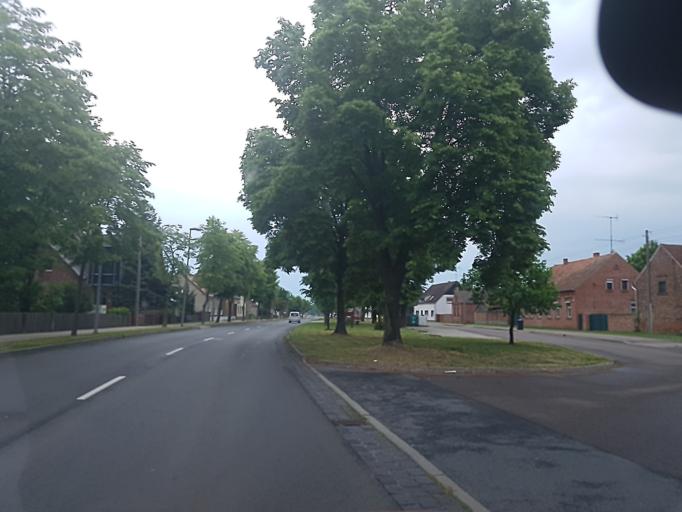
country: DE
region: Saxony-Anhalt
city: Holzdorf
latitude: 51.7788
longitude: 13.1295
